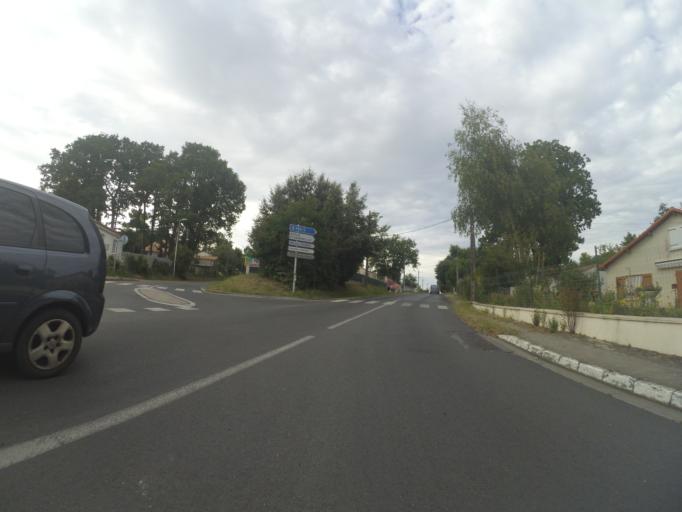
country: FR
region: Poitou-Charentes
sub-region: Departement de la Charente-Maritime
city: Meschers-sur-Gironde
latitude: 45.5657
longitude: -0.9613
